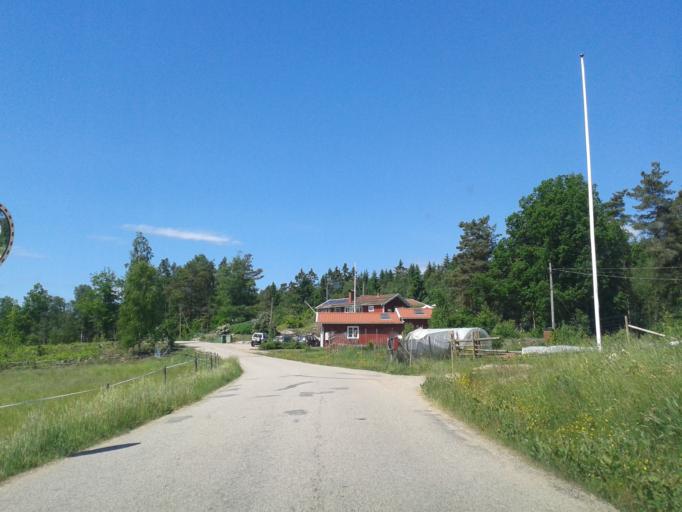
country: SE
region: Vaestra Goetaland
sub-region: Orust
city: Henan
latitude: 58.2810
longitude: 11.7394
